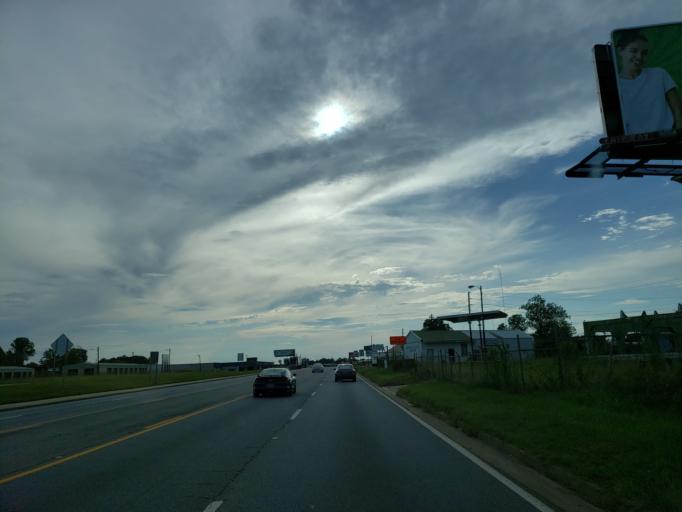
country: US
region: Georgia
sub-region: Tift County
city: Tifton
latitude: 31.4502
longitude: -83.4990
